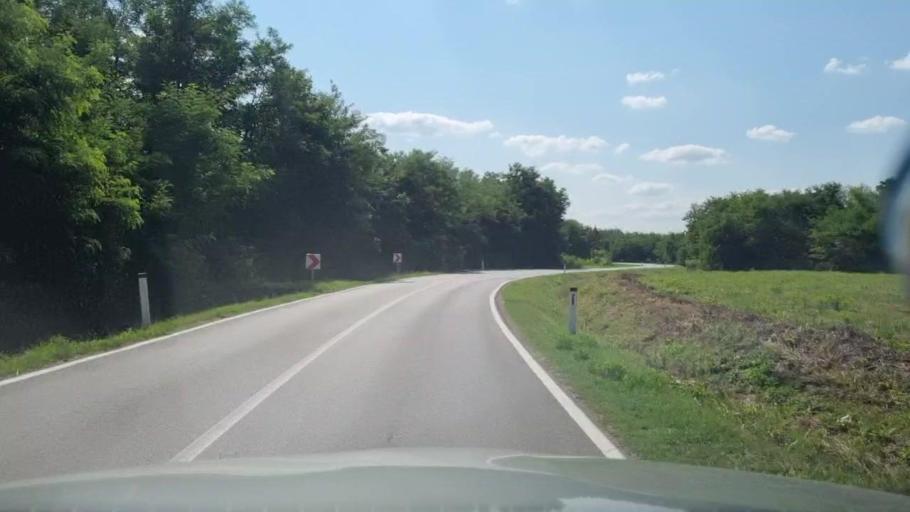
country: BA
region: Federation of Bosnia and Herzegovina
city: Odzak
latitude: 45.0266
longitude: 18.3458
